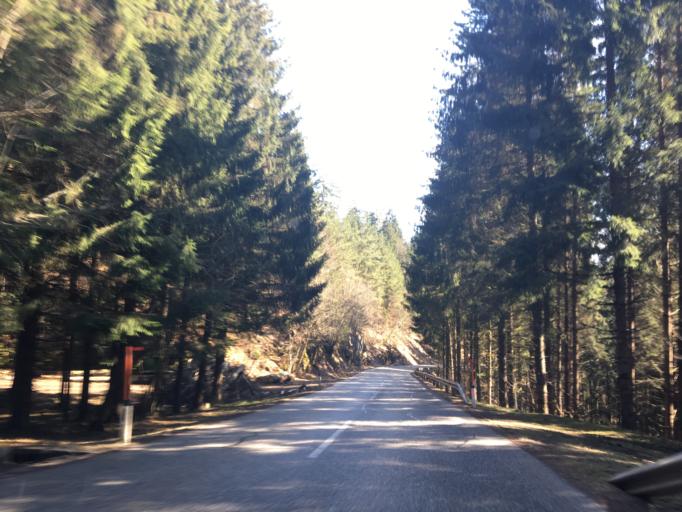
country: AT
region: Upper Austria
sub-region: Politischer Bezirk Perg
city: Sankt Georgen am Walde
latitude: 48.2809
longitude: 14.9050
